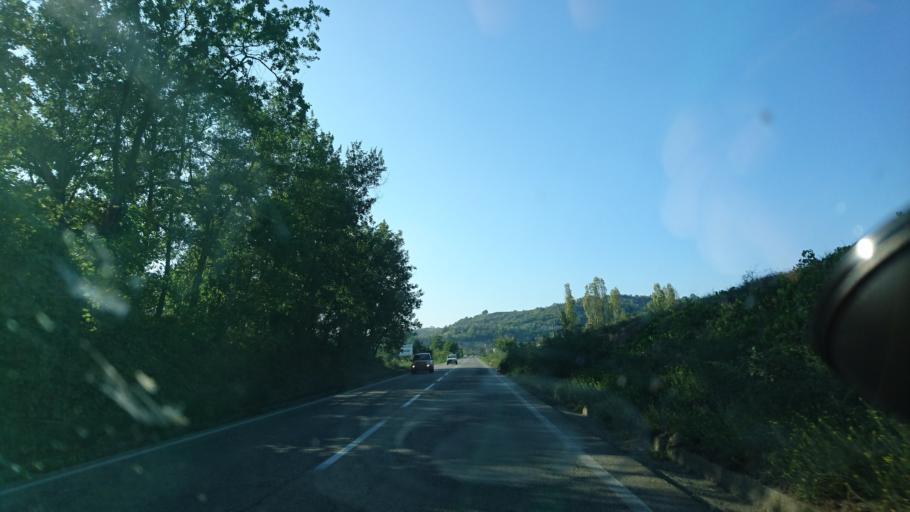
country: IT
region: Piedmont
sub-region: Provincia di Alessandria
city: Acqui Terme
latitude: 44.6725
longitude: 8.4452
